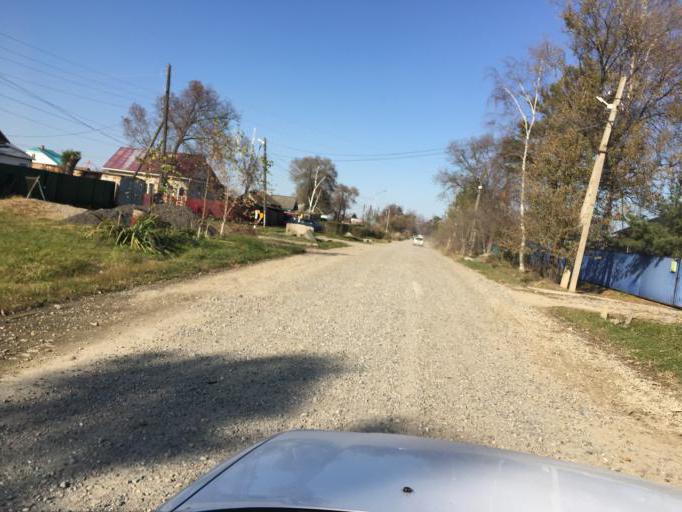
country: RU
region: Primorskiy
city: Dal'nerechensk
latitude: 45.9181
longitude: 133.7159
